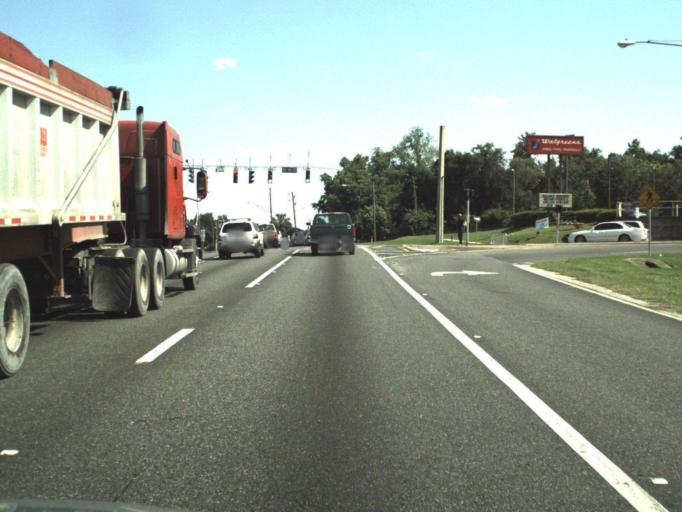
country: US
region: Florida
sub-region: Marion County
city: Belleview
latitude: 29.0630
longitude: -82.0669
